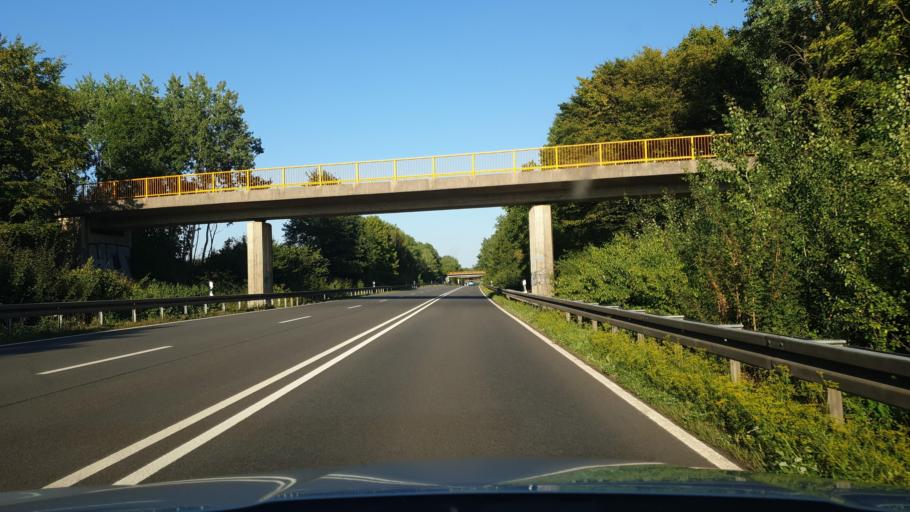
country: DE
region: Lower Saxony
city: Buckeburg
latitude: 52.2708
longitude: 9.0461
